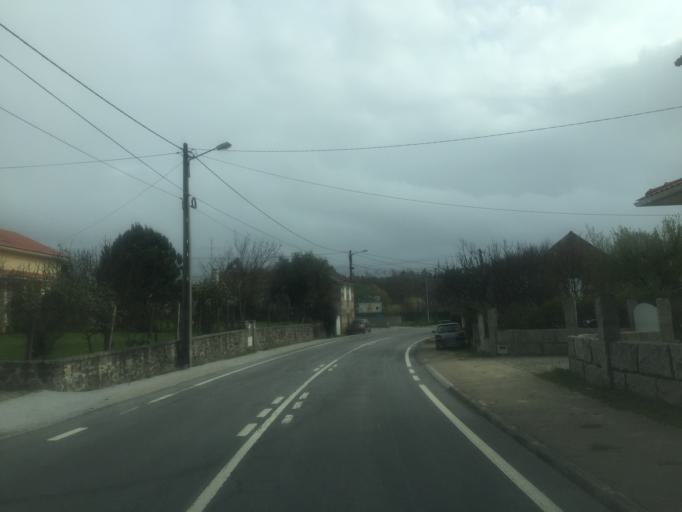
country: PT
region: Guarda
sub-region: Seia
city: Seia
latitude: 40.3991
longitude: -7.7413
